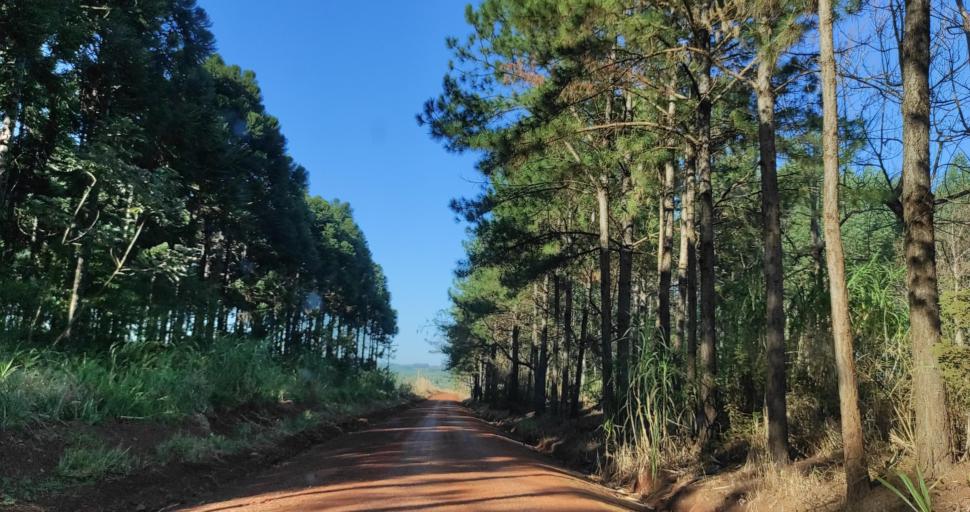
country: AR
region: Misiones
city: Puerto Rico
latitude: -26.8620
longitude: -55.0267
